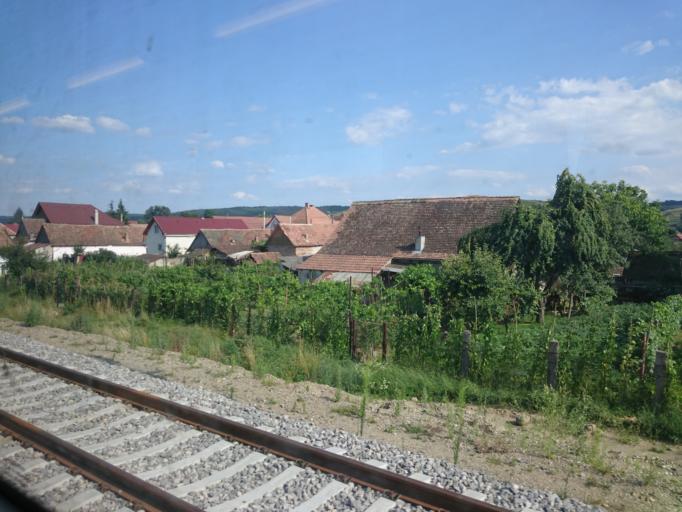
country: RO
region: Mures
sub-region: Comuna Danes
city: Danes
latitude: 46.2239
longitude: 24.6905
